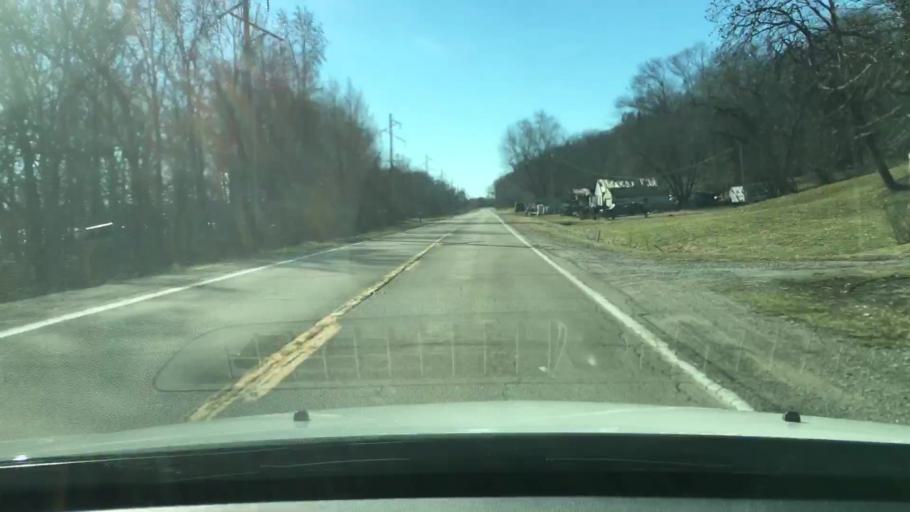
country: US
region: Illinois
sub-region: Fulton County
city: Astoria
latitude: 40.1936
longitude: -90.2049
